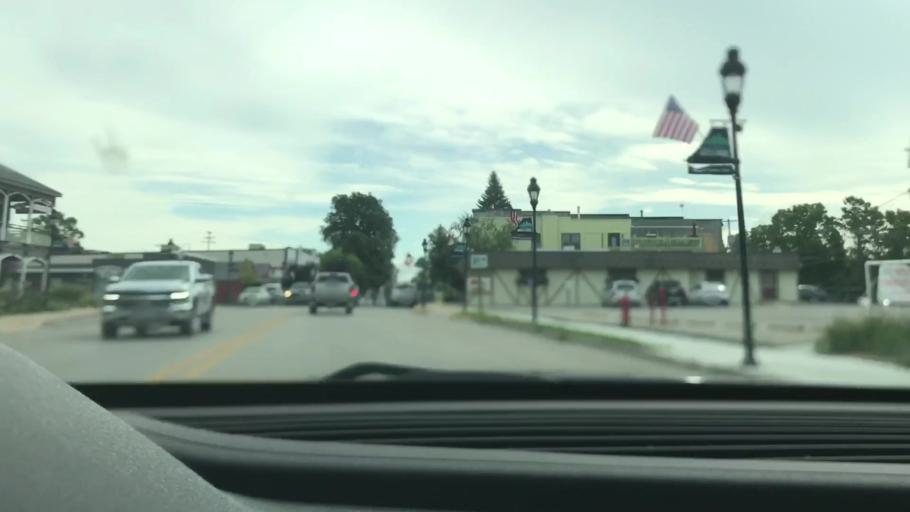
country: US
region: Michigan
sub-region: Antrim County
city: Bellaire
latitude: 44.9783
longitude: -85.2101
